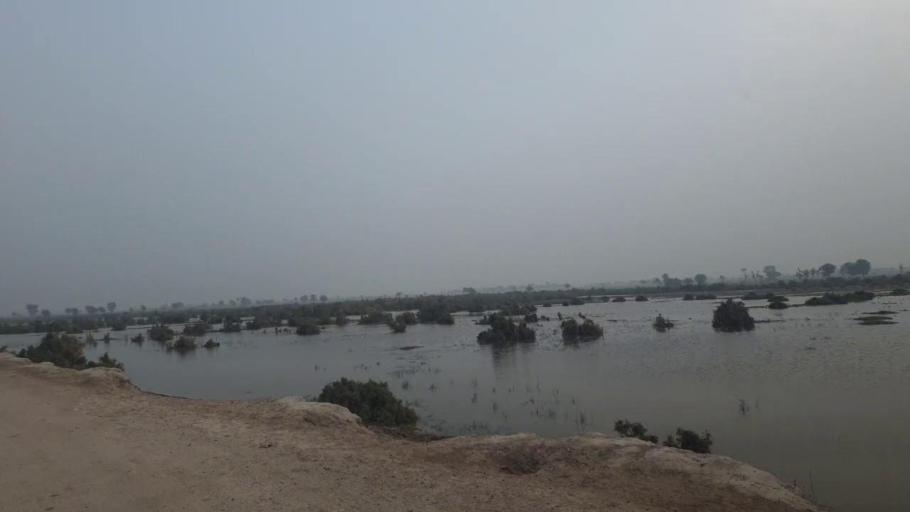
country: PK
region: Sindh
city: Tando Adam
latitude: 25.7853
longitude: 68.7086
